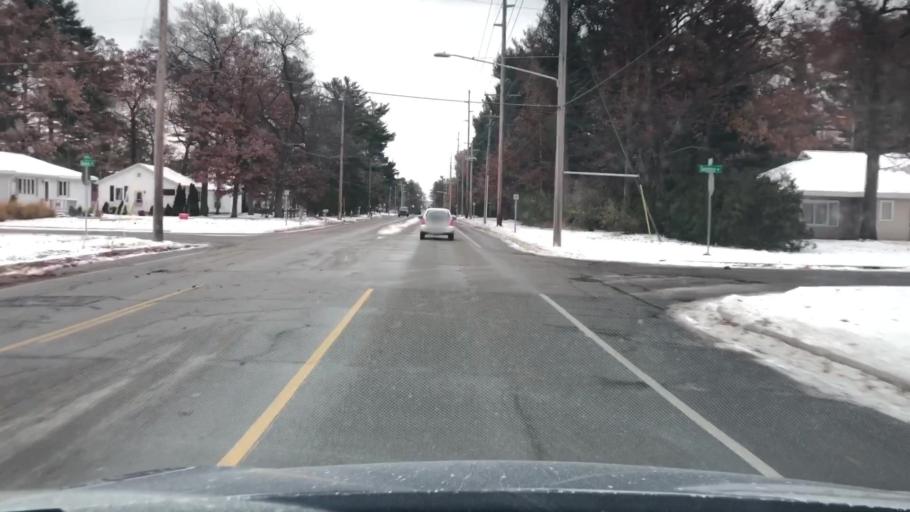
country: US
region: Michigan
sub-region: Grand Traverse County
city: Traverse City
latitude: 44.7586
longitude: -85.5843
